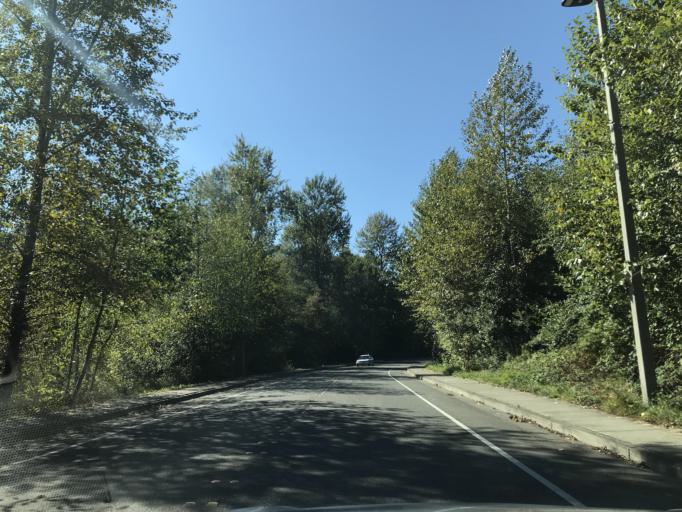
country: US
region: Washington
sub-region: Whatcom County
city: Bellingham
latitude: 48.7969
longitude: -122.5052
